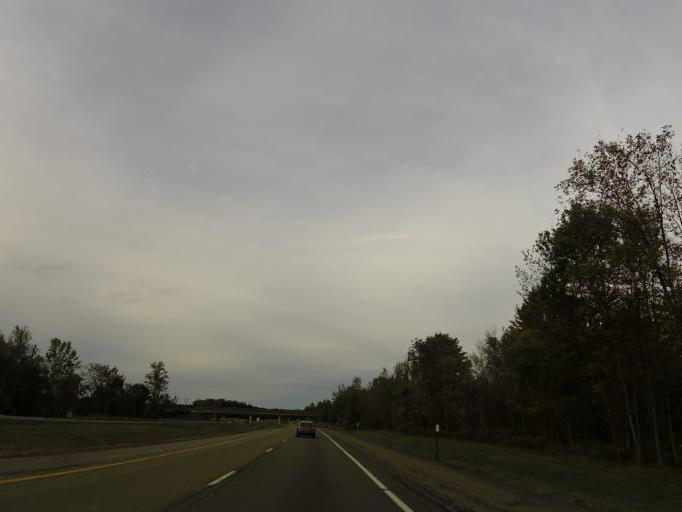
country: US
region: New York
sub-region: Erie County
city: Lake Erie Beach
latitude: 42.5912
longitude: -79.0521
